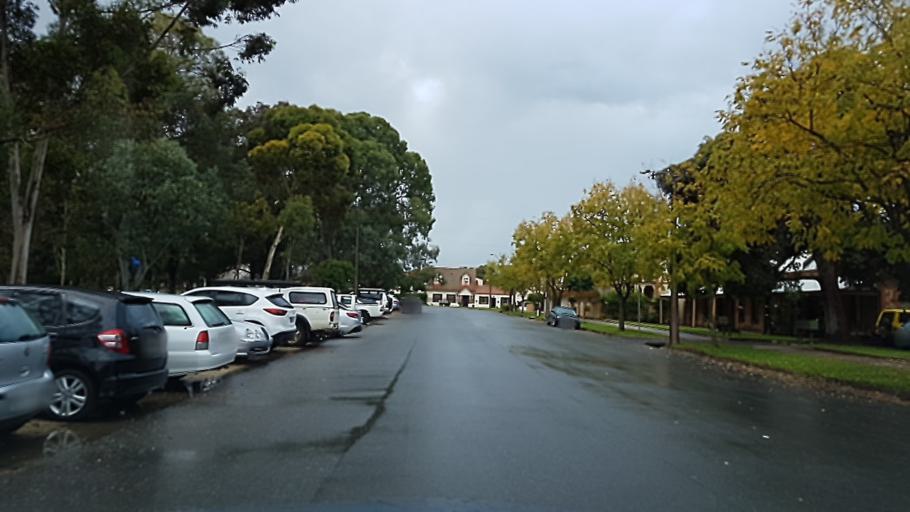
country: AU
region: South Australia
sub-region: Adelaide
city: North Adelaide
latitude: -34.9048
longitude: 138.6063
